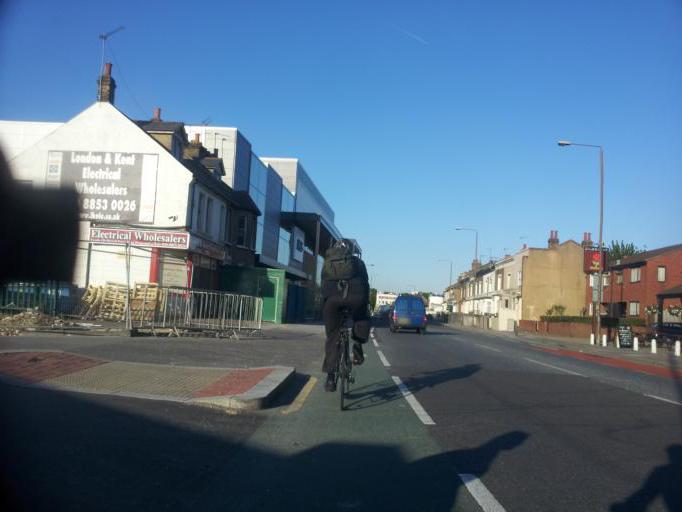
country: GB
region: England
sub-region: Greater London
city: Blackheath
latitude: 51.4872
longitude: 0.0253
